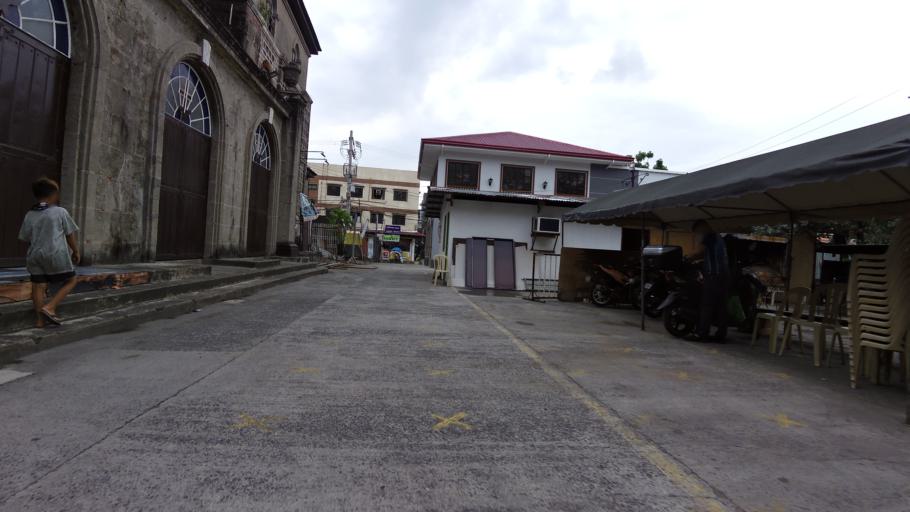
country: PH
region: Metro Manila
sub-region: San Juan
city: San Juan
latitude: 14.5820
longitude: 121.0136
